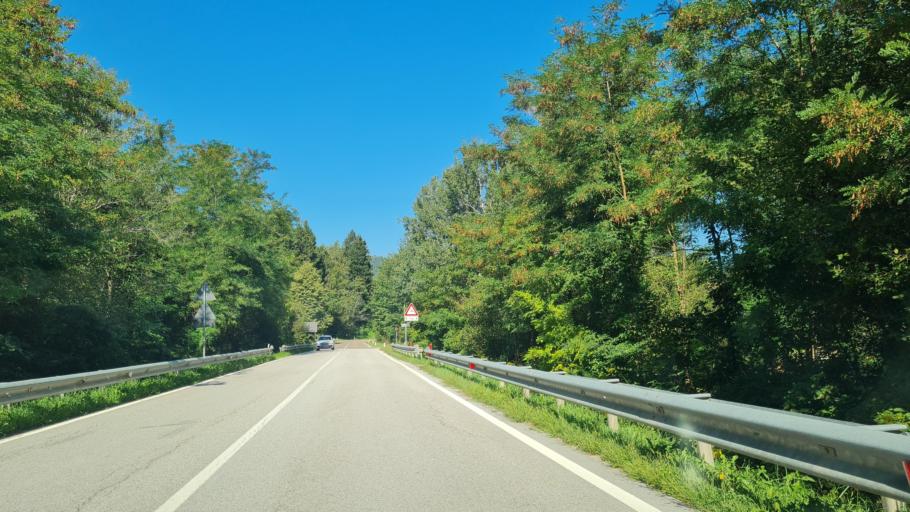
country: IT
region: Trentino-Alto Adige
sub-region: Provincia di Trento
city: Caldonazzo
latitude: 45.9853
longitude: 11.2783
